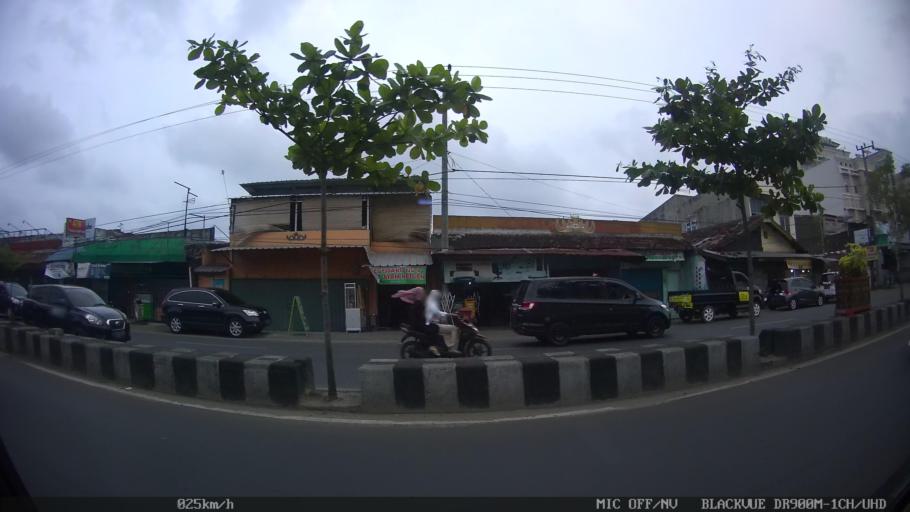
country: ID
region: Lampung
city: Bandarlampung
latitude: -5.4083
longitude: 105.2711
